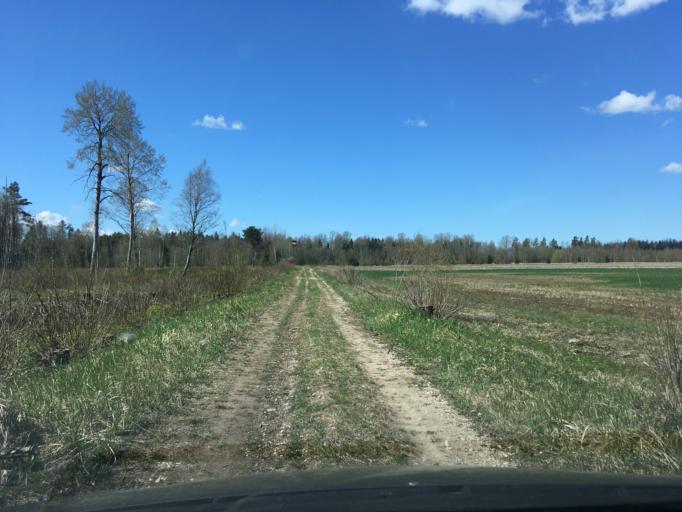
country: EE
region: Harju
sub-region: Raasiku vald
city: Arukula
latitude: 59.2052
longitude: 25.1290
